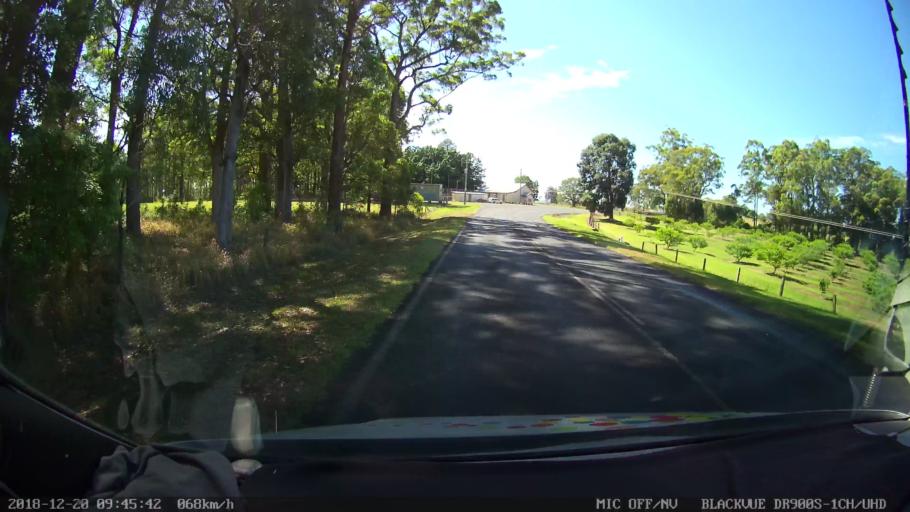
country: AU
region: New South Wales
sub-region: Lismore Municipality
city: Lismore
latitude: -28.7460
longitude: 153.3021
